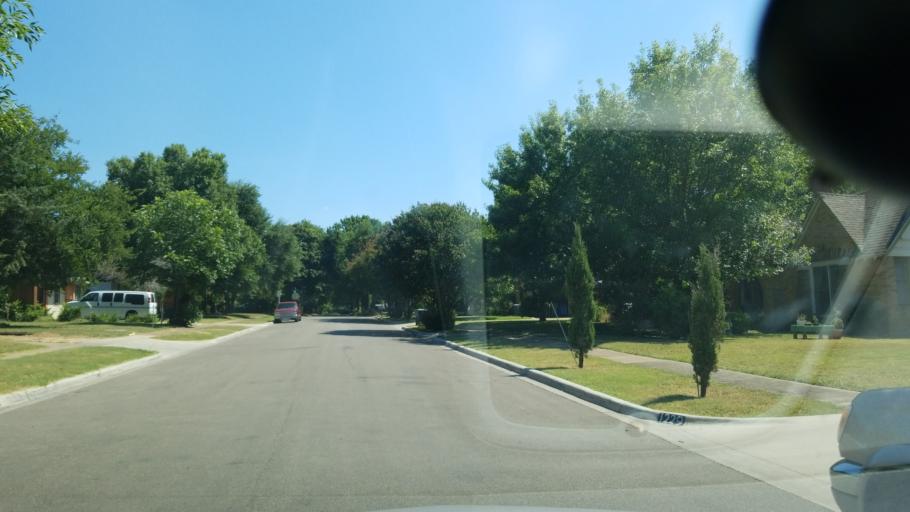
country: US
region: Texas
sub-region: Dallas County
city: Cockrell Hill
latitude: 32.7324
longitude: -96.8543
